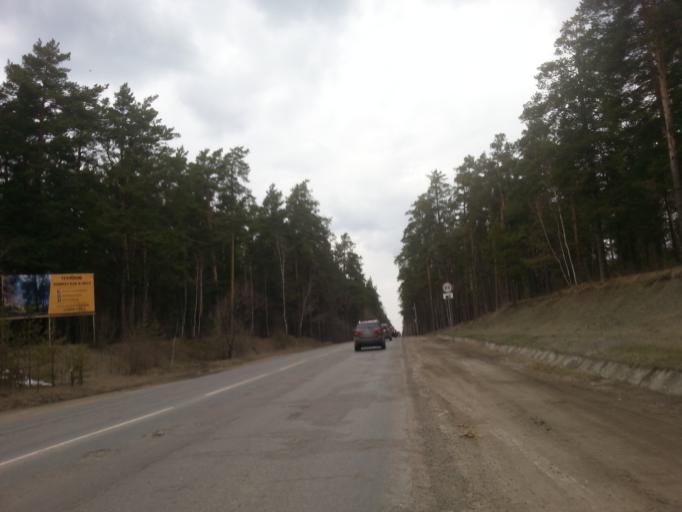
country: RU
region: Altai Krai
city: Yuzhnyy
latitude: 53.2710
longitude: 83.7244
